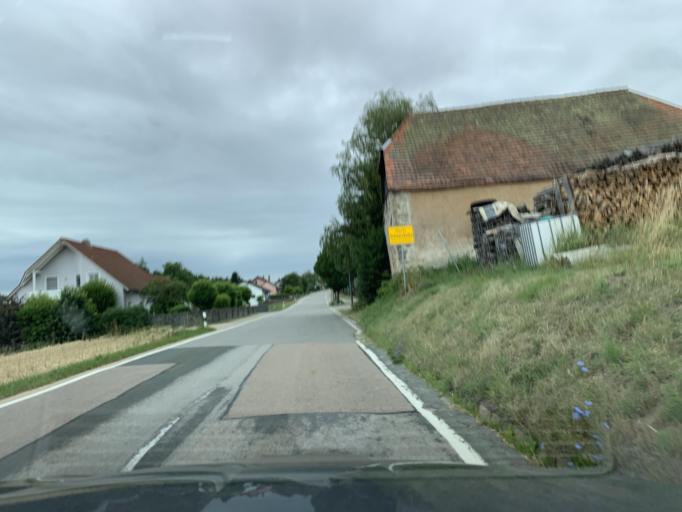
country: DE
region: Bavaria
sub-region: Upper Palatinate
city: Schwarzhofen
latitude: 49.3725
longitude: 12.3479
